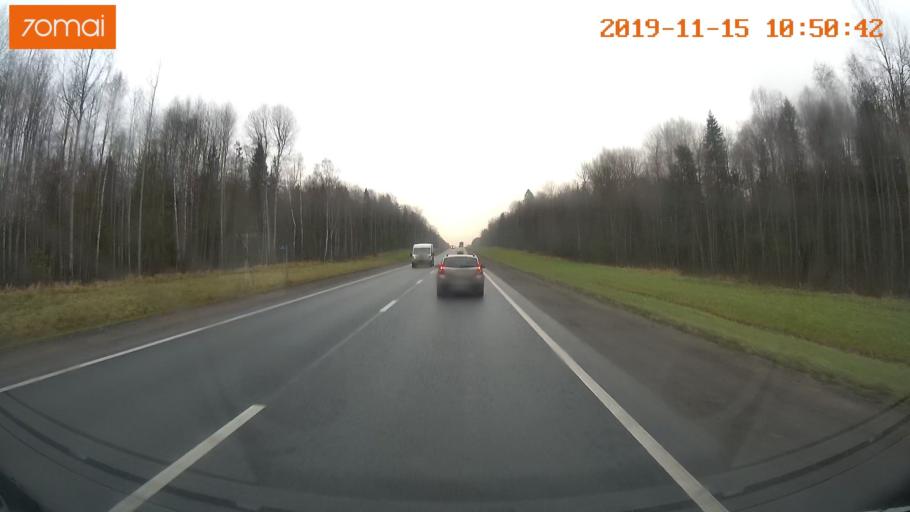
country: RU
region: Vologda
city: Chebsara
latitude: 59.1840
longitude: 38.6876
